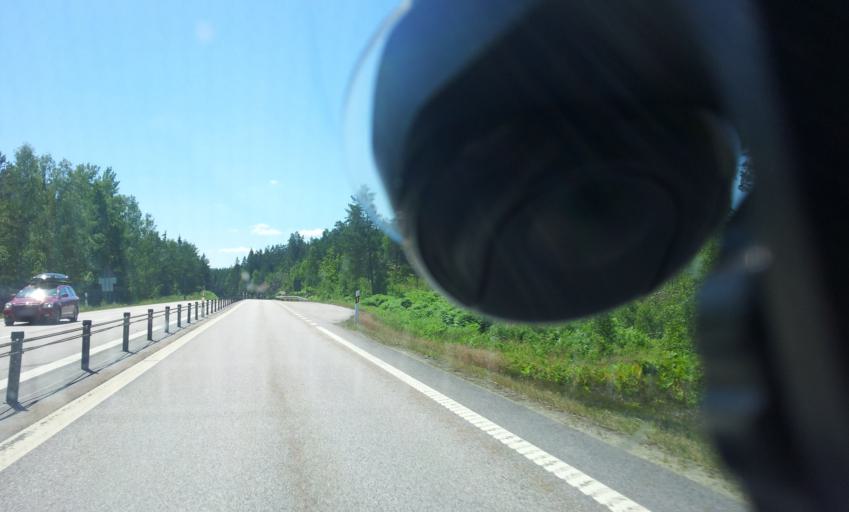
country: SE
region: Kalmar
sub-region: Vasterviks Kommun
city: Forserum
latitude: 58.0401
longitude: 16.5207
